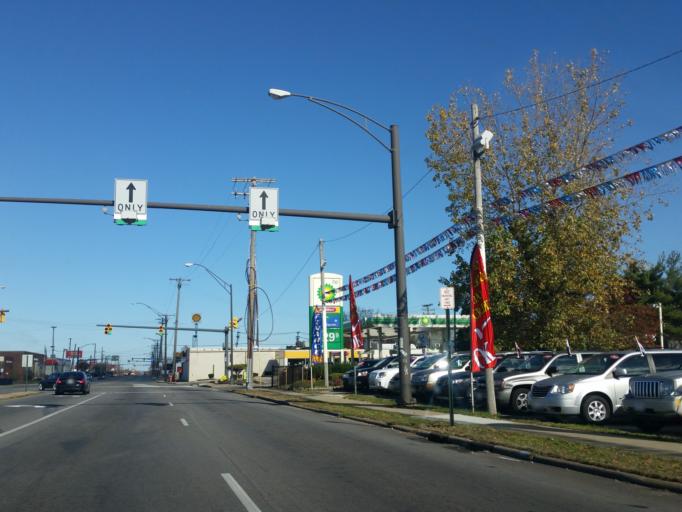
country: US
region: Ohio
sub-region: Cuyahoga County
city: Lakewood
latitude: 41.4683
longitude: -81.7687
